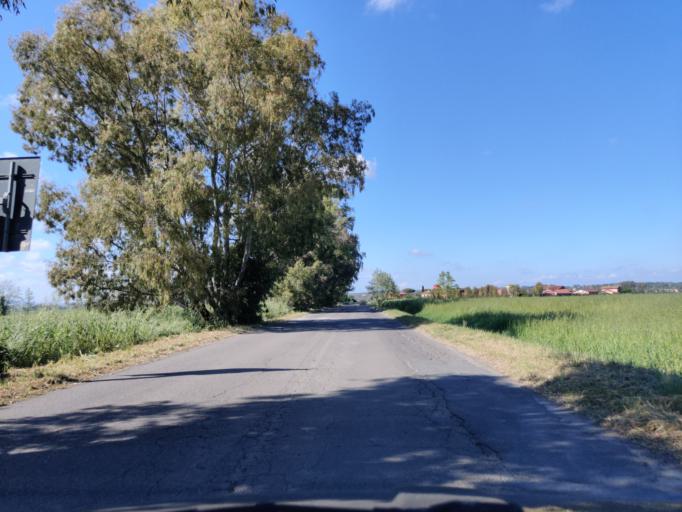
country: IT
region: Latium
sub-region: Citta metropolitana di Roma Capitale
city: Maccarese
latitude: 41.8784
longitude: 12.2138
